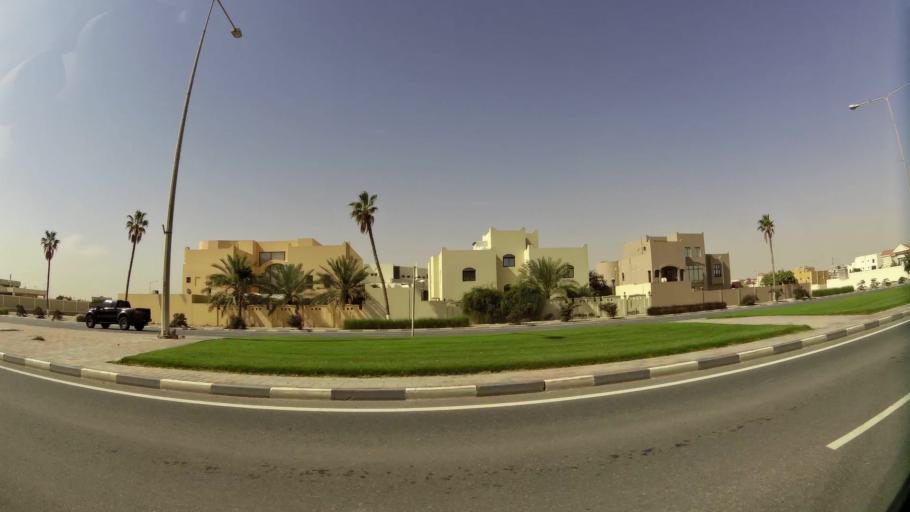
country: QA
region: Baladiyat ad Dawhah
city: Doha
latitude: 25.3521
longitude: 51.4994
